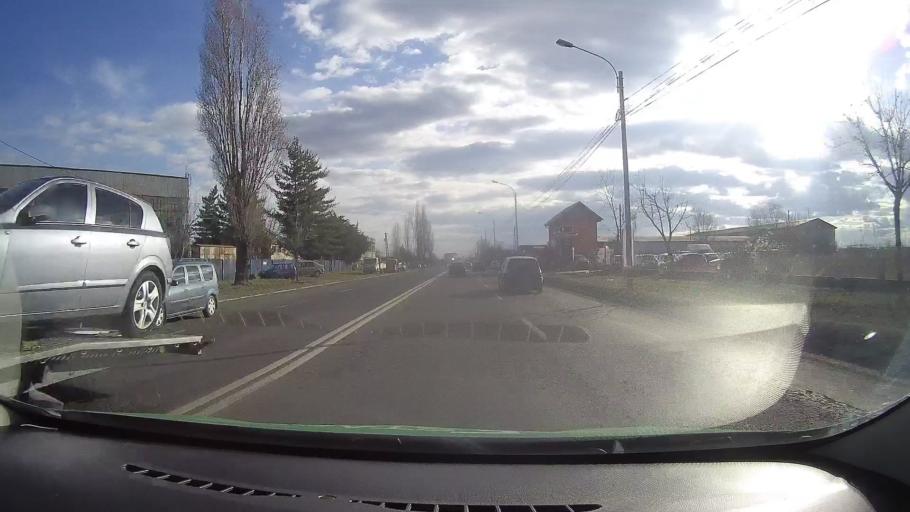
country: RO
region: Dambovita
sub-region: Comuna Lucieni
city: Lucieni
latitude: 44.8471
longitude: 25.4443
